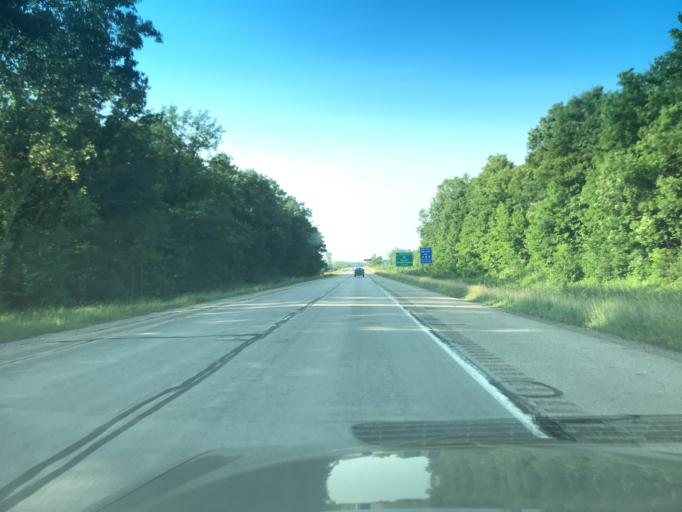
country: US
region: Michigan
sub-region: Ingham County
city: Holt
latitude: 42.6485
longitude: -84.4770
